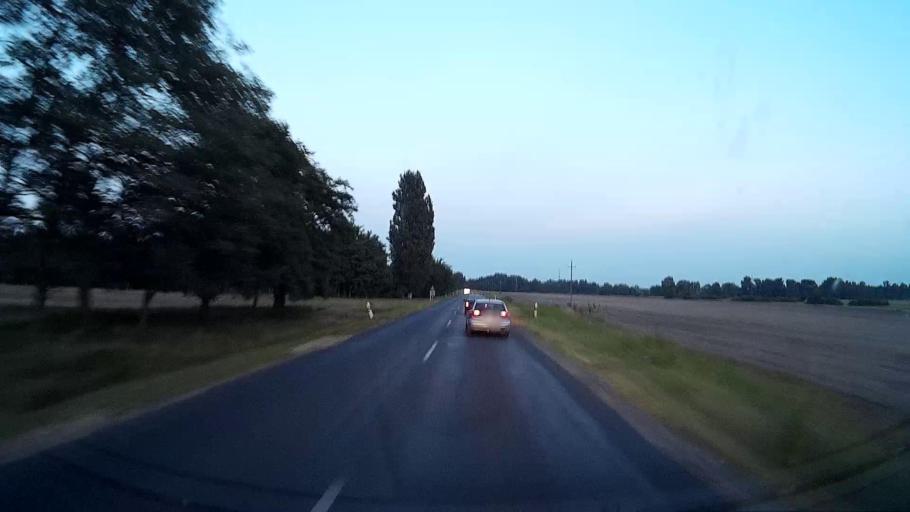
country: HU
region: Pest
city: Cegledbercel
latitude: 47.2086
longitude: 19.6864
